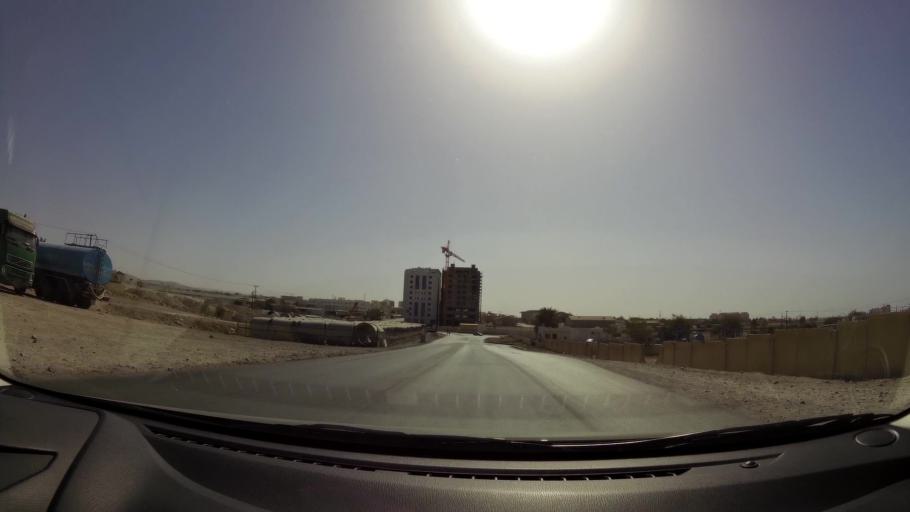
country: OM
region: Muhafazat Masqat
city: Bawshar
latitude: 23.5802
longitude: 58.3600
